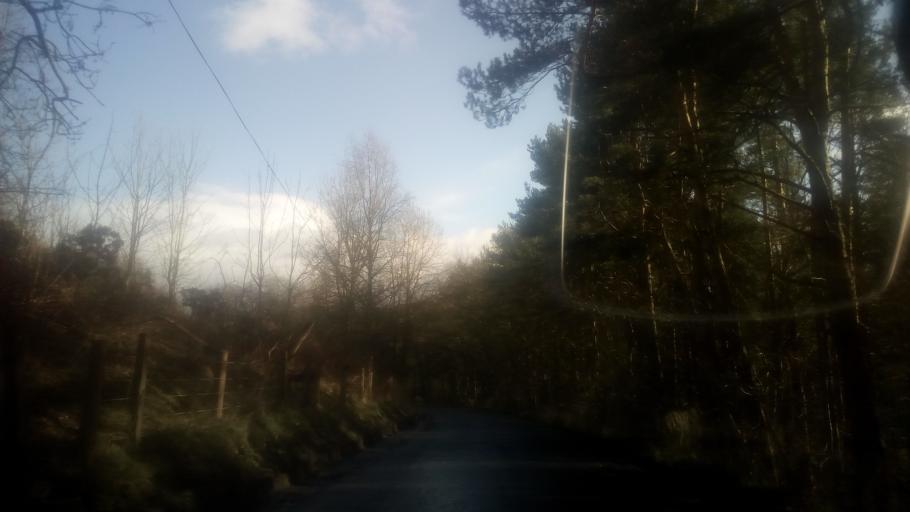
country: GB
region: Scotland
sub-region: The Scottish Borders
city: Hawick
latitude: 55.4138
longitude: -2.8499
